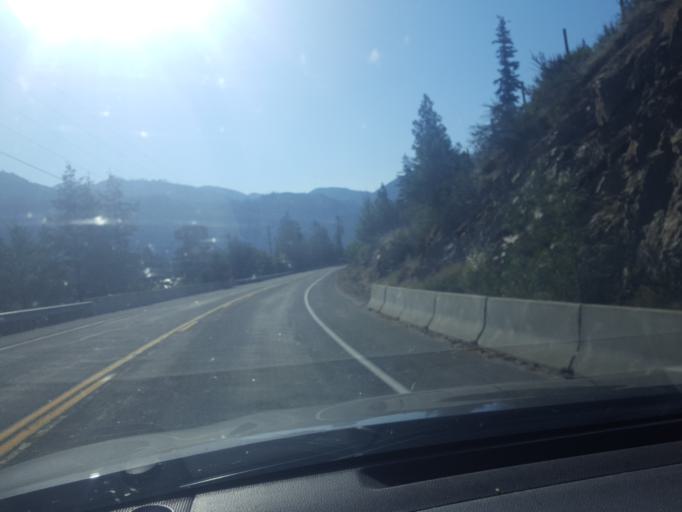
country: US
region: Washington
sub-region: Chelan County
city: Granite Falls
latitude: 47.9887
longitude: -120.2416
